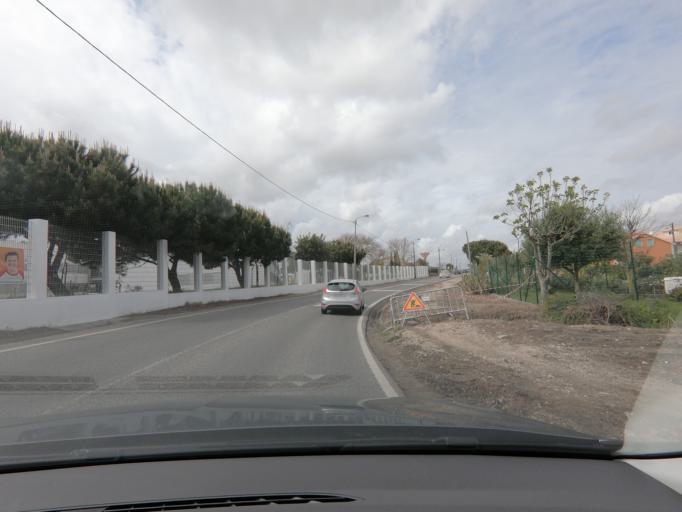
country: PT
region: Lisbon
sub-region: Cascais
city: Sao Domingos de Rana
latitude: 38.7162
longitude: -9.3396
